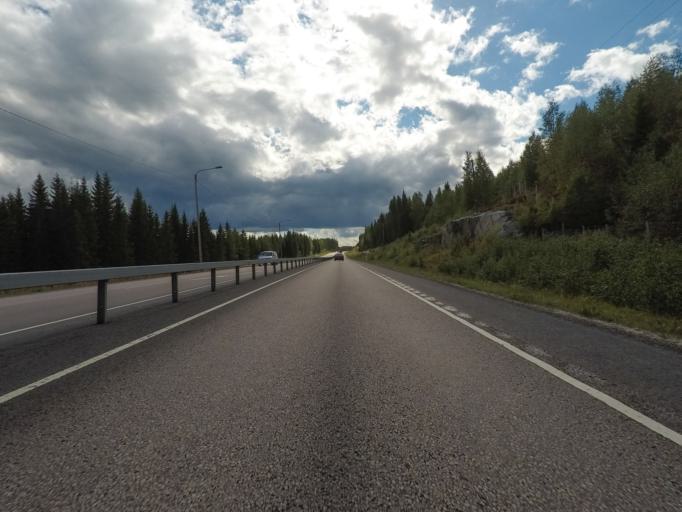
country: FI
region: Central Finland
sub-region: Jyvaeskylae
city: Toivakka
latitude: 62.0235
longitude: 26.0475
